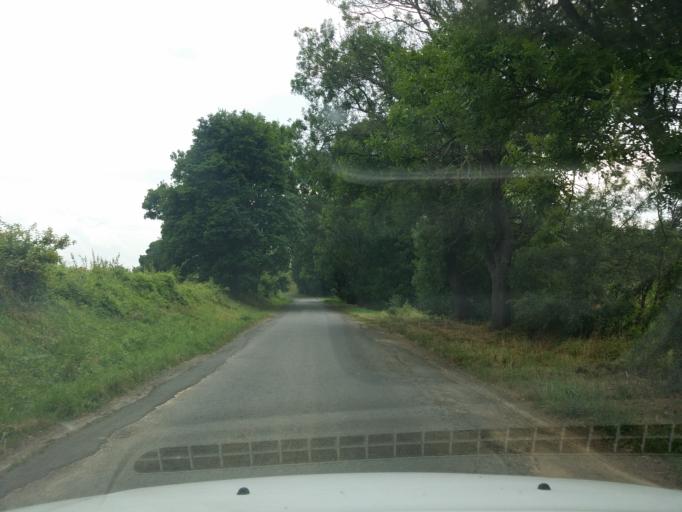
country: HU
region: Nograd
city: Bercel
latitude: 47.9761
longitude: 19.3621
